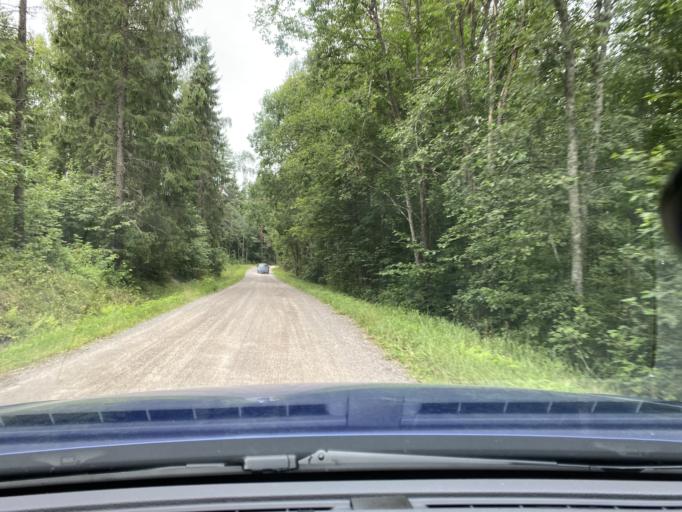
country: FI
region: Pirkanmaa
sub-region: Ylae-Pirkanmaa
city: Maenttae
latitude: 62.0229
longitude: 24.7224
